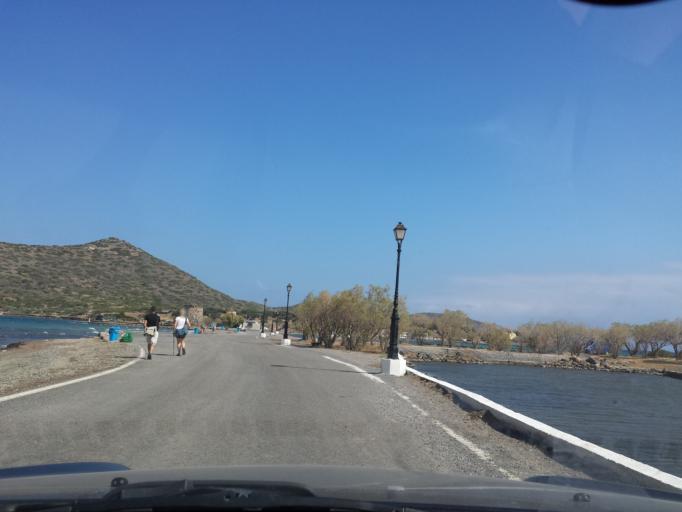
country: GR
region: Crete
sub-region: Nomos Lasithiou
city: Skhisma
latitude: 35.2570
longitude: 25.7328
